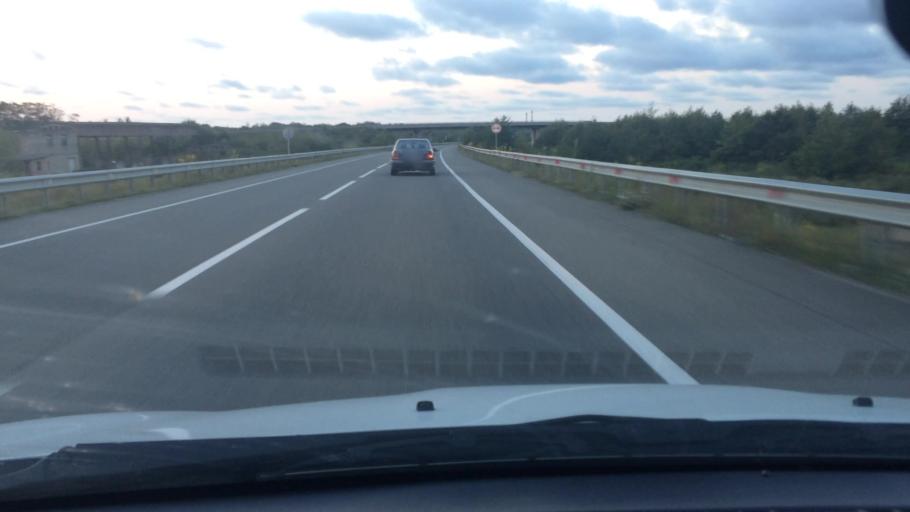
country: GE
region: Guria
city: Urek'i
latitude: 41.9153
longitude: 41.7778
